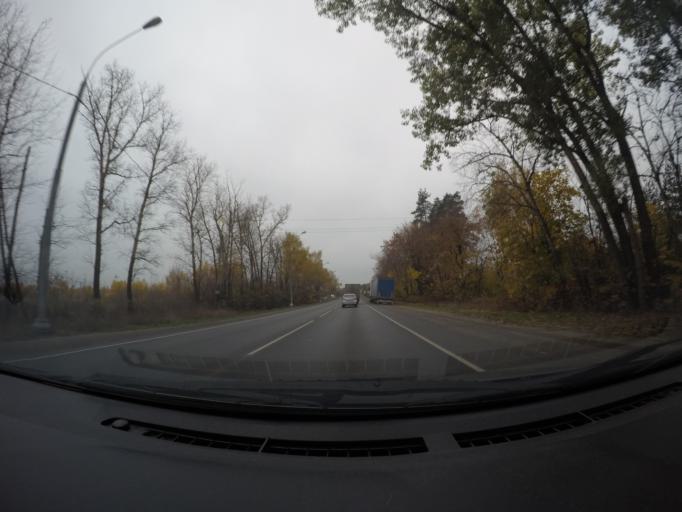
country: RU
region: Moskovskaya
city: Malyshevo
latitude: 55.4707
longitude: 38.3404
